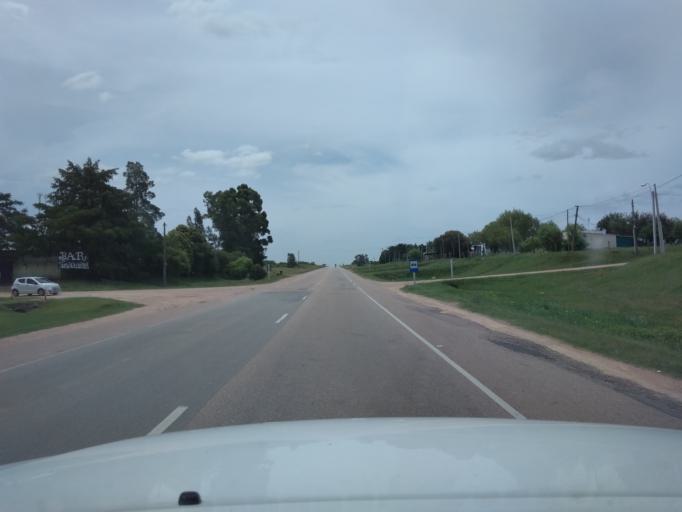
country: UY
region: Canelones
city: Canelones
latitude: -34.4955
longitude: -56.2819
